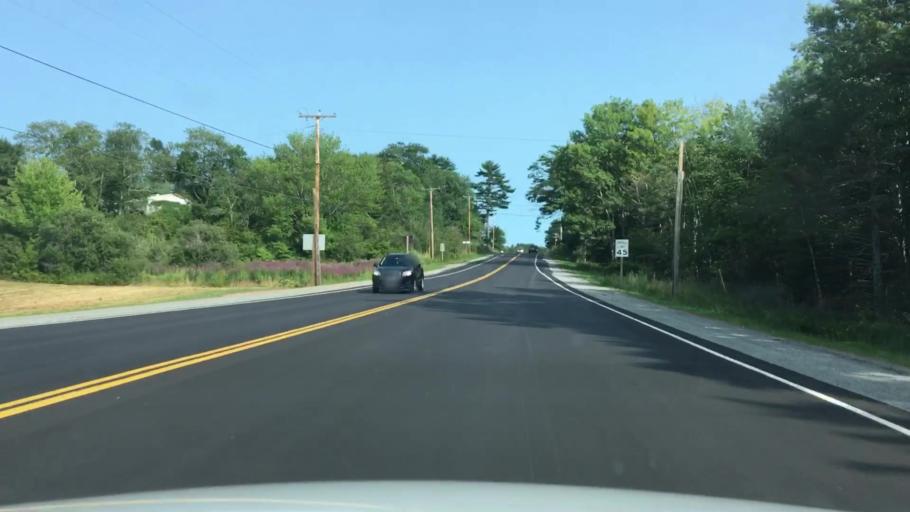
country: US
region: Maine
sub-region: Knox County
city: Warren
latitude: 44.1162
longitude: -69.2626
